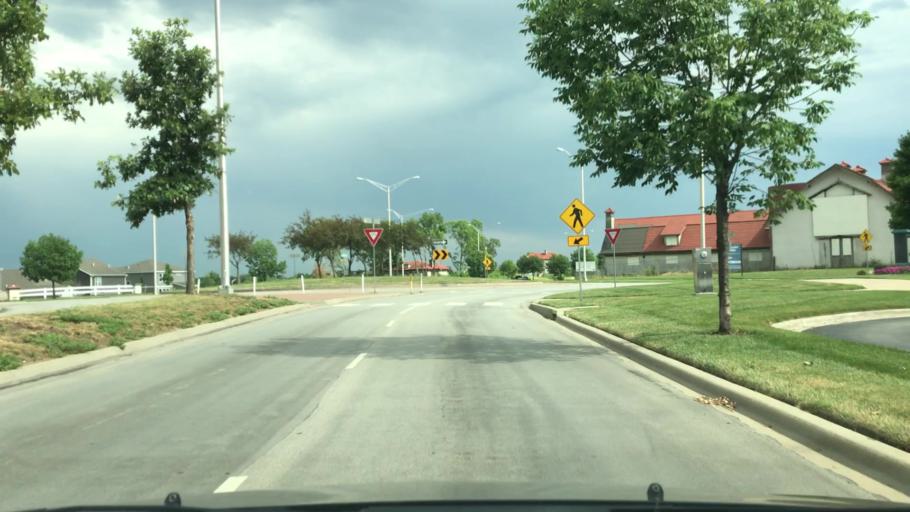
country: US
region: Missouri
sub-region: Jackson County
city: Lees Summit
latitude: 38.9094
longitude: -94.4480
